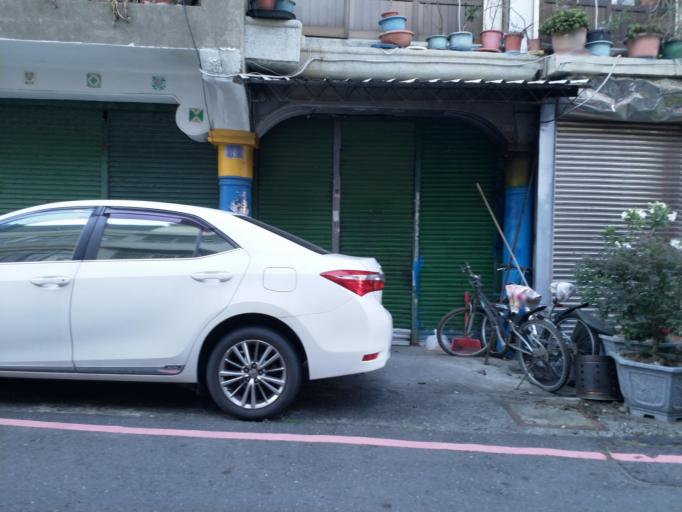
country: TW
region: Taiwan
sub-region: Pingtung
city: Pingtung
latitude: 22.8981
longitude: 120.5460
